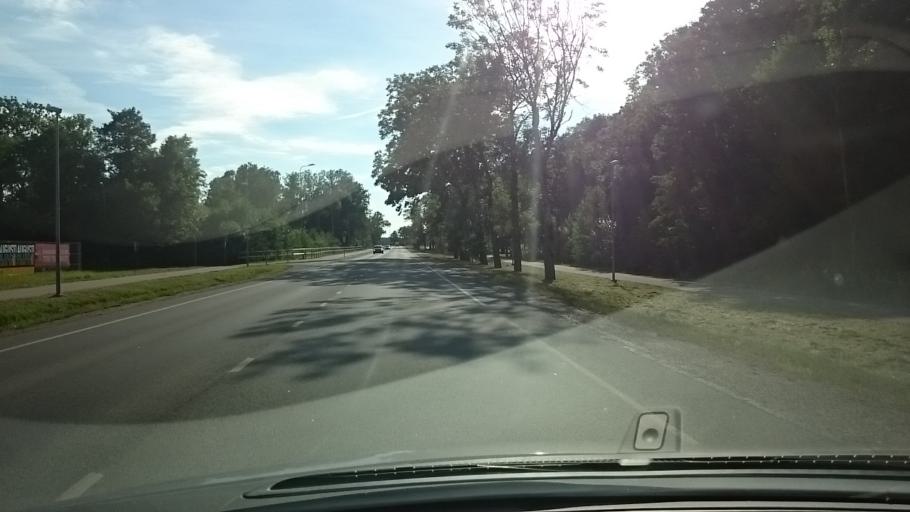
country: EE
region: Laeaene
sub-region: Ridala Parish
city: Uuemoisa
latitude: 58.9431
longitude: 23.5899
